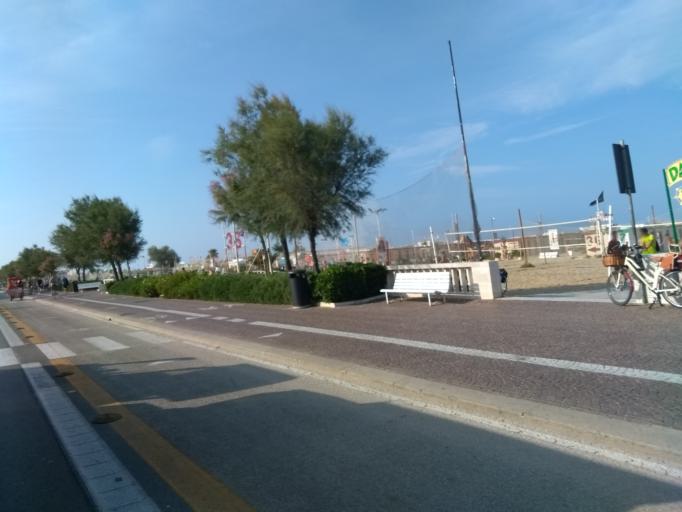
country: IT
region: Emilia-Romagna
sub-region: Provincia di Rimini
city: Rimini
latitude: 44.0649
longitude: 12.5853
